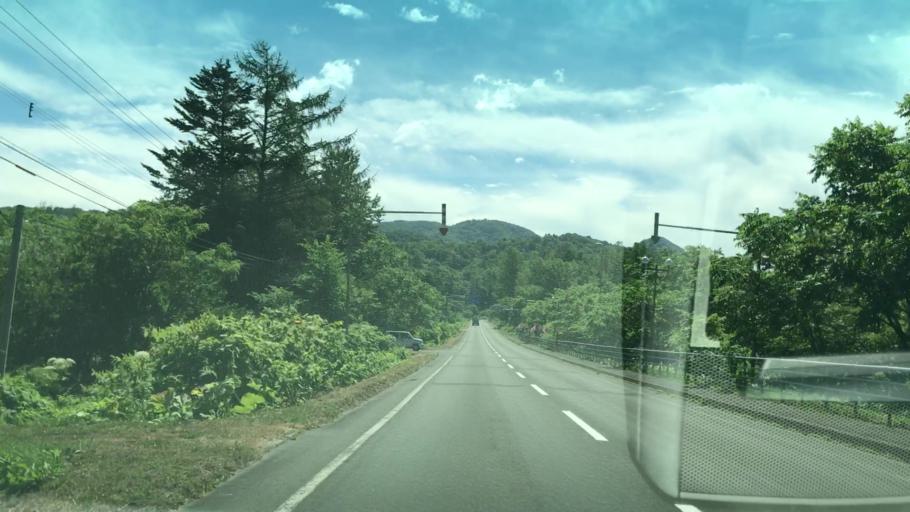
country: JP
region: Hokkaido
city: Shimo-furano
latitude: 42.9525
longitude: 142.4366
